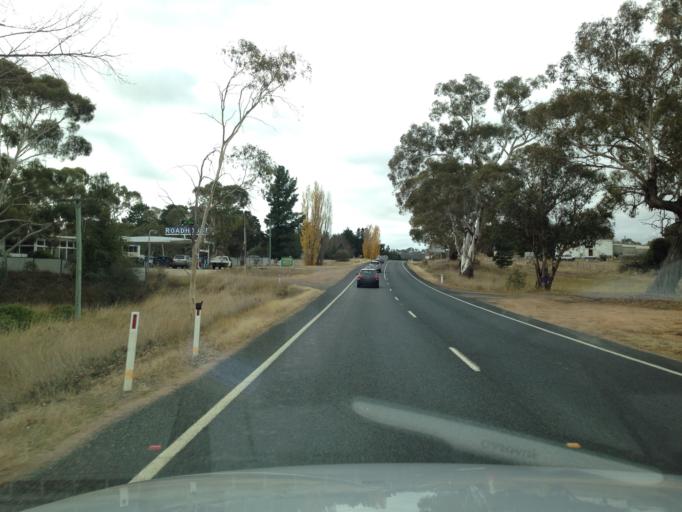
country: AU
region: New South Wales
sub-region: Cooma-Monaro
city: Cooma
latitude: -36.2457
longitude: 149.0542
